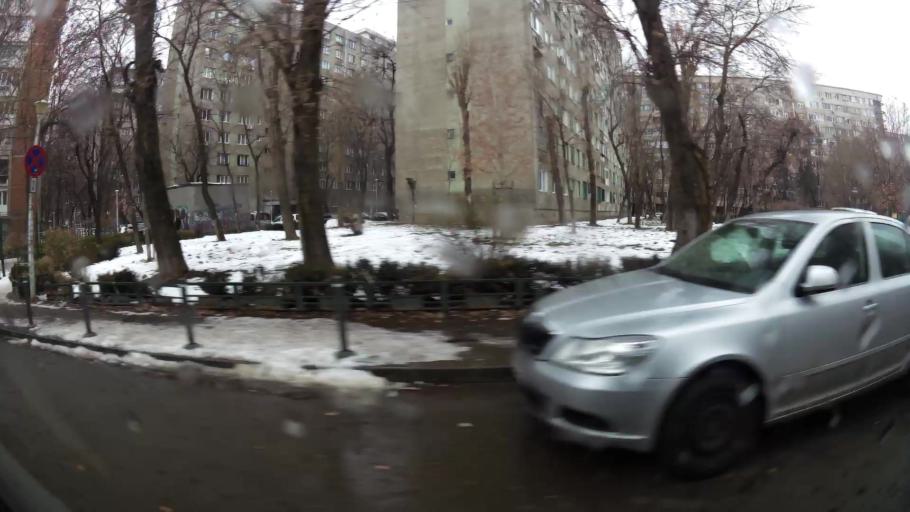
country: RO
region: Ilfov
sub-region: Comuna Chiajna
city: Rosu
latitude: 44.4151
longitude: 26.0266
